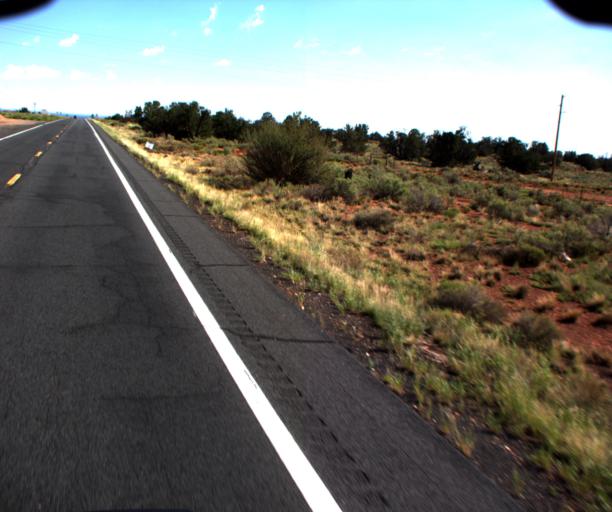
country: US
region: Arizona
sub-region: Coconino County
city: Williams
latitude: 35.6425
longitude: -112.1408
